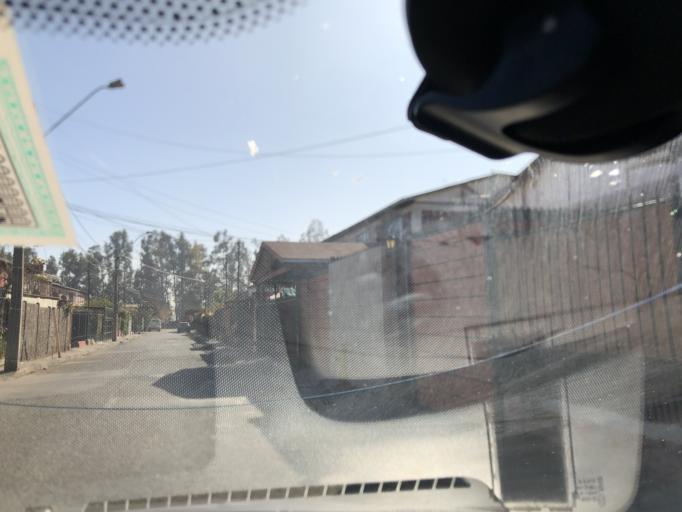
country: CL
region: Santiago Metropolitan
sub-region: Provincia de Cordillera
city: Puente Alto
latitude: -33.5783
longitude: -70.5854
